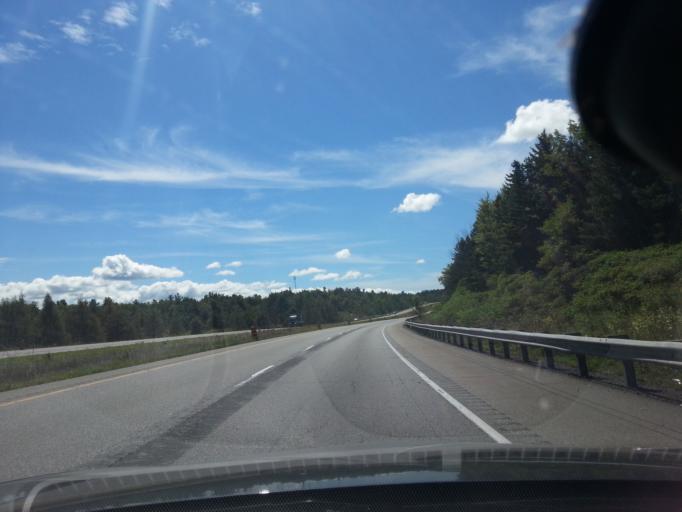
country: US
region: New York
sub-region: Jefferson County
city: Alexandria Bay
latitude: 44.4325
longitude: -75.8954
